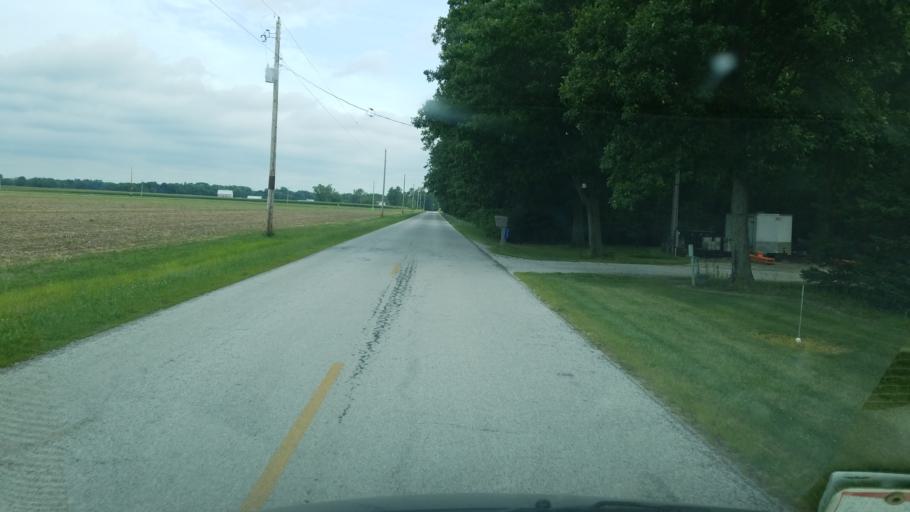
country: US
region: Ohio
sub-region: Sandusky County
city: Green Springs
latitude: 41.1784
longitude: -83.1030
